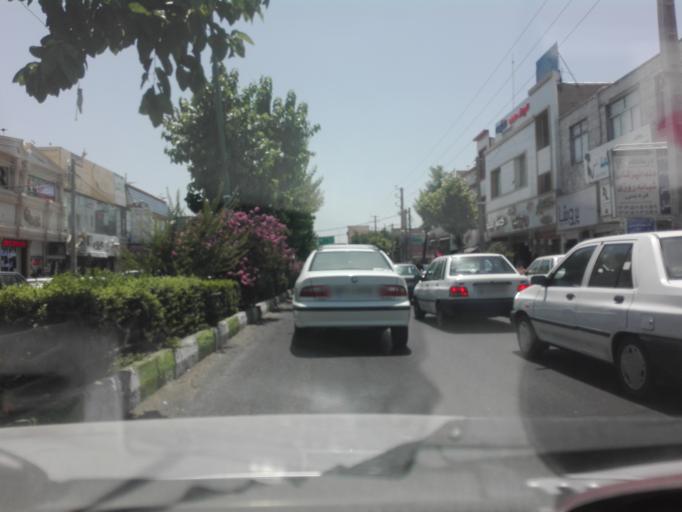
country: IR
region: Tehran
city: Shahre Jadide Andisheh
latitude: 35.7264
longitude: 50.9889
